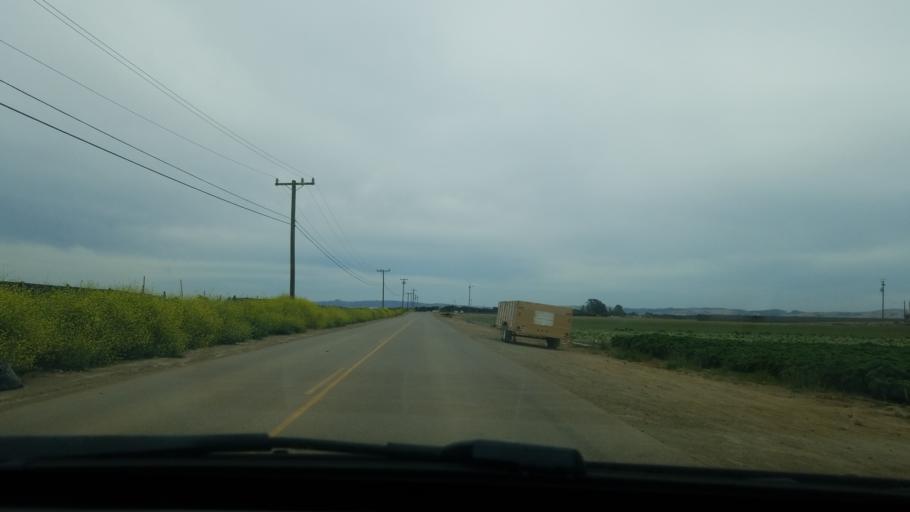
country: US
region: California
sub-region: San Luis Obispo County
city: Nipomo
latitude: 34.9997
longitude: -120.5167
